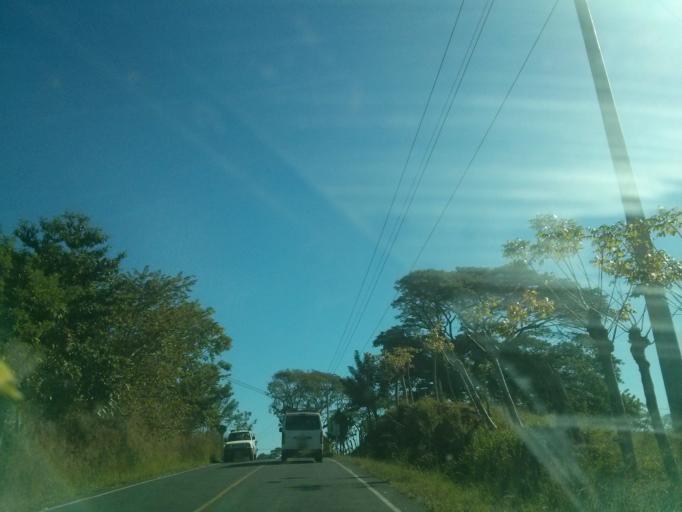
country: CR
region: Puntarenas
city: Paquera
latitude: 9.7001
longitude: -85.0575
